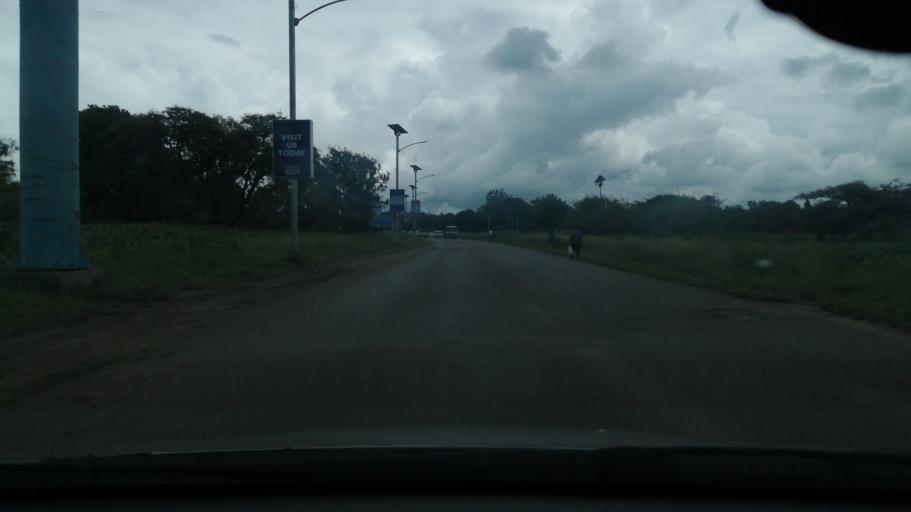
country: ZW
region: Harare
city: Harare
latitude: -17.8018
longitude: 31.0751
